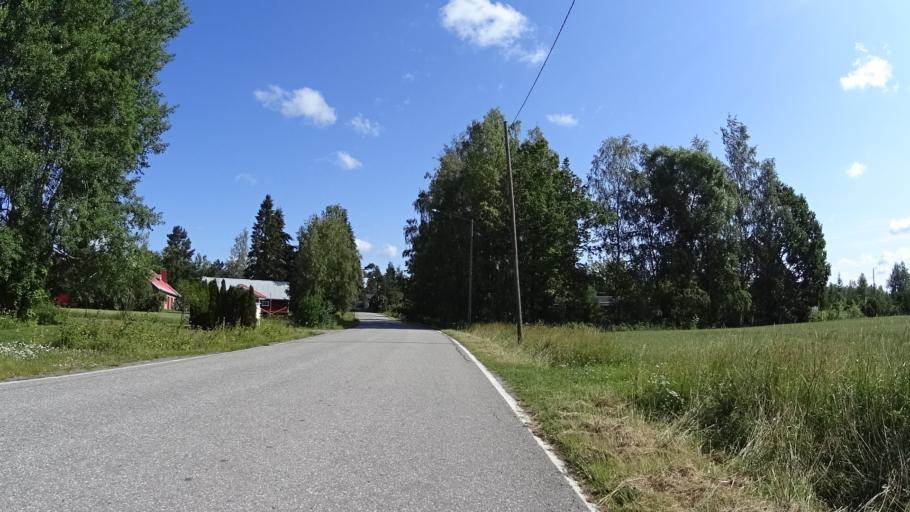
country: FI
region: Uusimaa
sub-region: Helsinki
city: Jaervenpaeae
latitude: 60.4376
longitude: 25.0658
